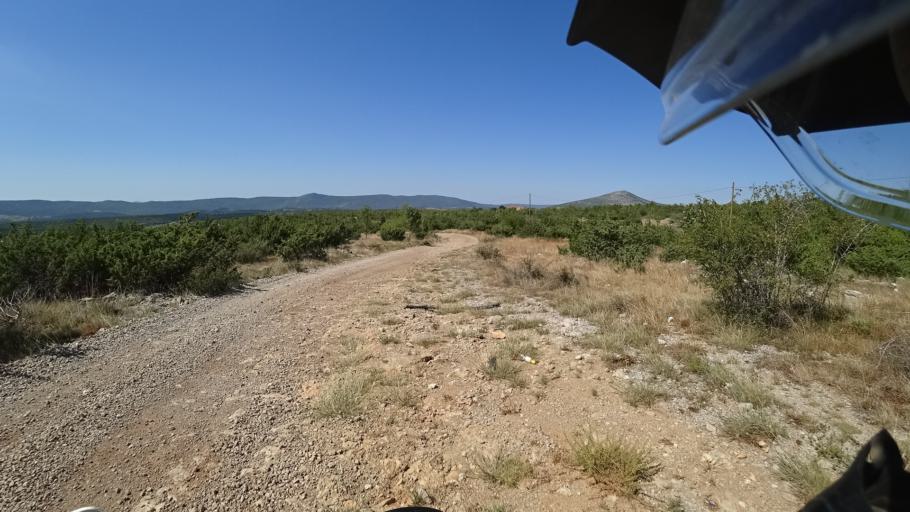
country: HR
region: Splitsko-Dalmatinska
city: Hrvace
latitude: 43.7529
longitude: 16.4471
